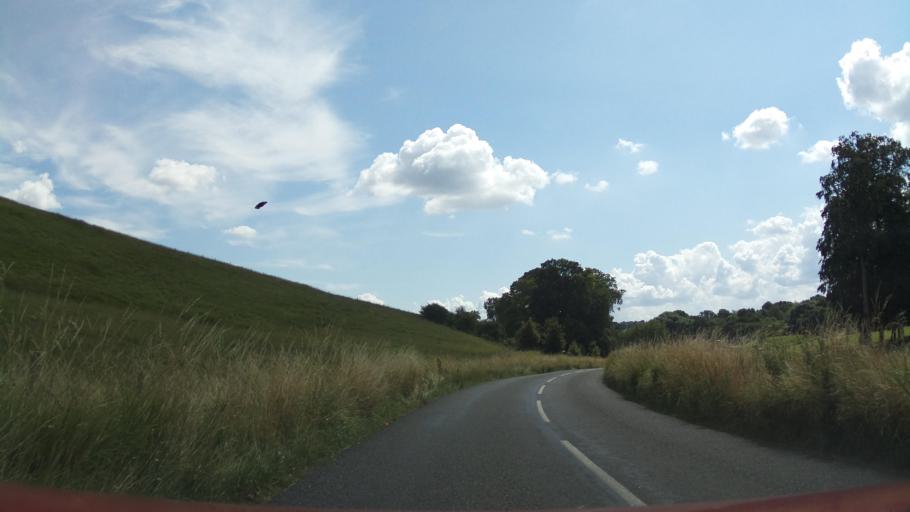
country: GB
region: England
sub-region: Wiltshire
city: Aldbourne
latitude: 51.5316
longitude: -1.5865
